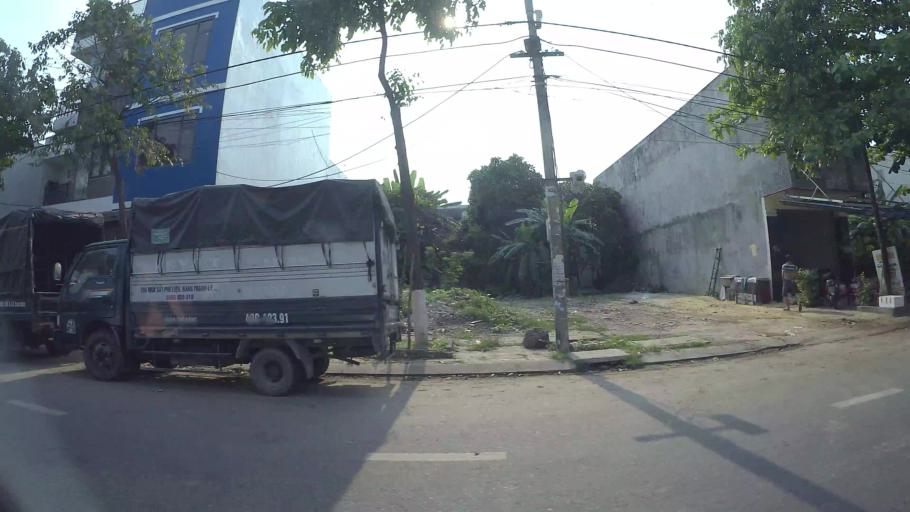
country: VN
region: Da Nang
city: Lien Chieu
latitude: 16.0543
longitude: 108.1726
